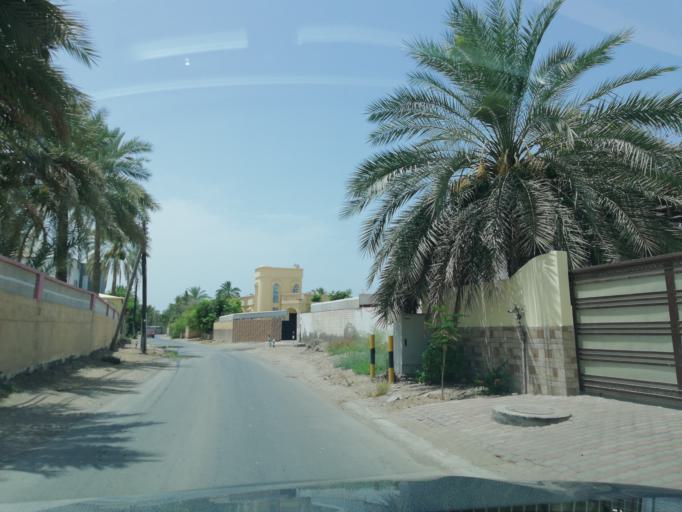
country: OM
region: Muhafazat Masqat
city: As Sib al Jadidah
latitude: 23.6605
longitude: 58.2094
